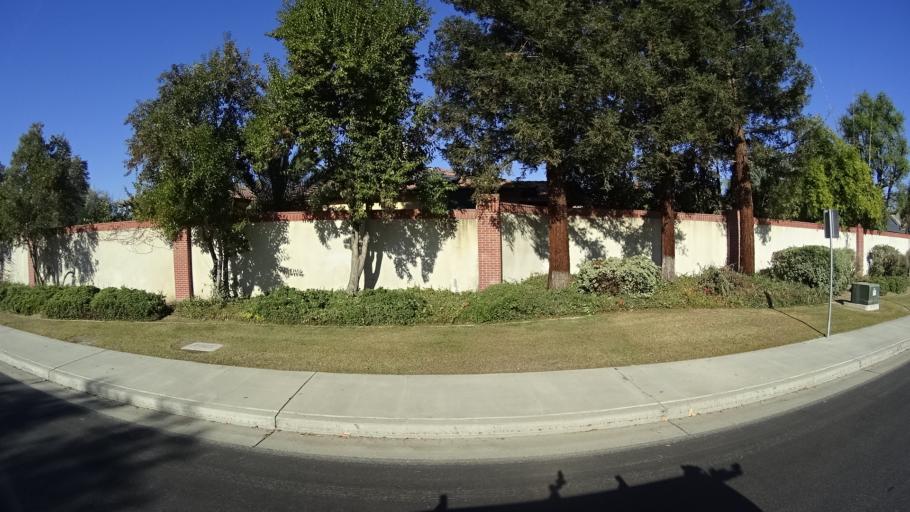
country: US
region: California
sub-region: Kern County
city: Greenacres
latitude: 35.3284
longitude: -119.1205
